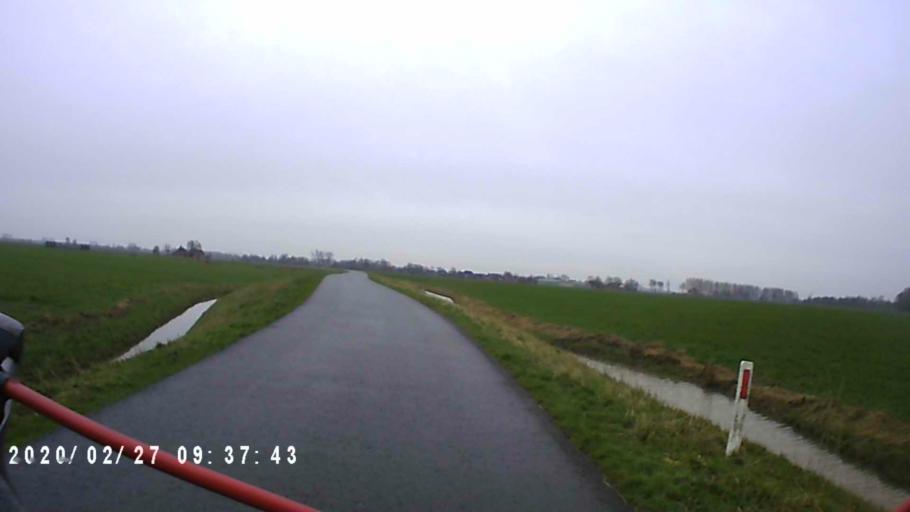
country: NL
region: Groningen
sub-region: Gemeente Zuidhorn
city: Noordhorn
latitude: 53.2816
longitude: 6.4291
